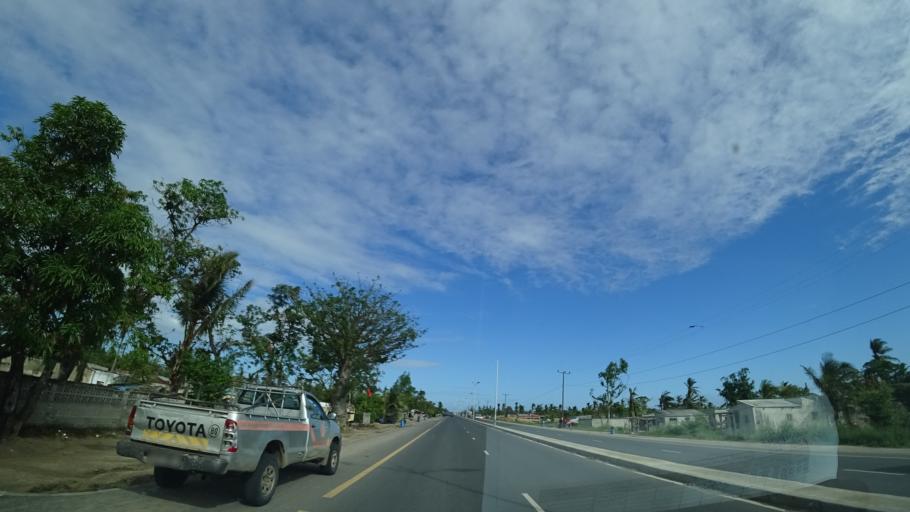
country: MZ
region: Sofala
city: Beira
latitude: -19.7555
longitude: 34.8773
